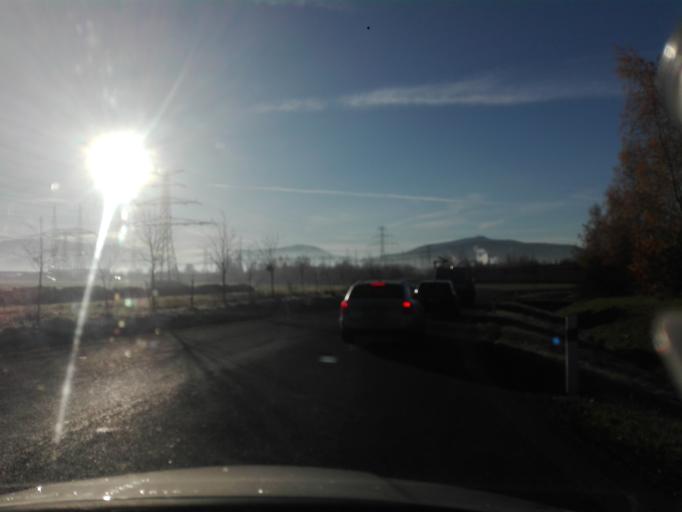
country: CZ
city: Dobra
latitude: 49.6756
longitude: 18.4266
